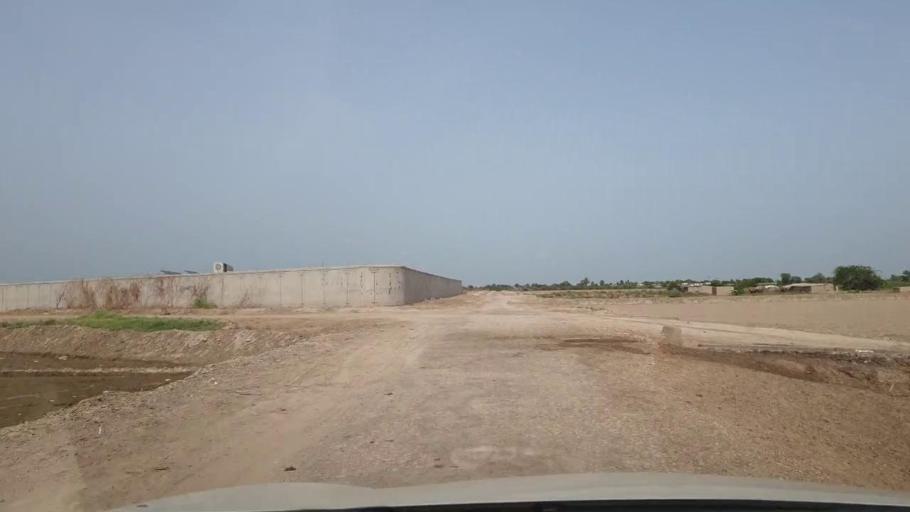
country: PK
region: Sindh
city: Mirwah Gorchani
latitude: 25.2778
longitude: 68.9481
